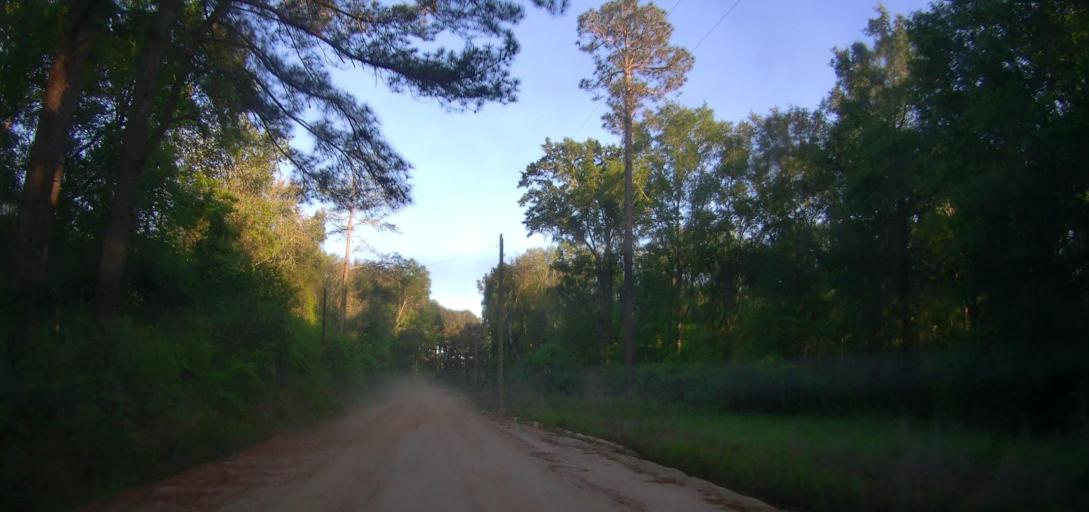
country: US
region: Georgia
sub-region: Irwin County
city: Ocilla
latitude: 31.6494
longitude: -83.2272
